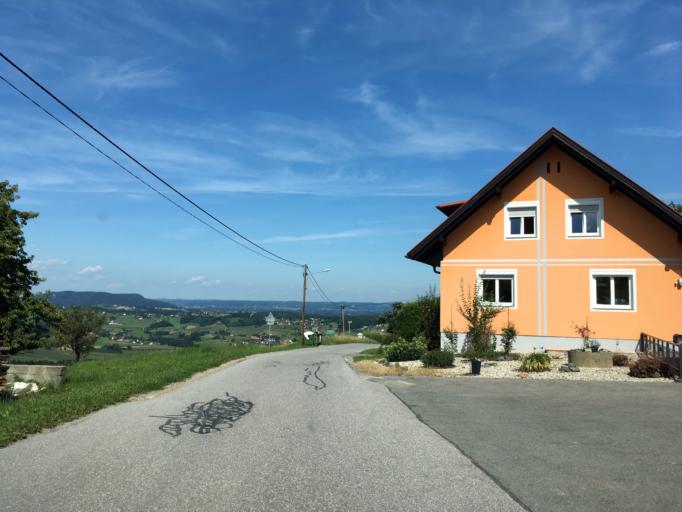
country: AT
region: Styria
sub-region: Politischer Bezirk Leibnitz
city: Sankt Nikolai im Sausal
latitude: 46.8042
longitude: 15.4383
